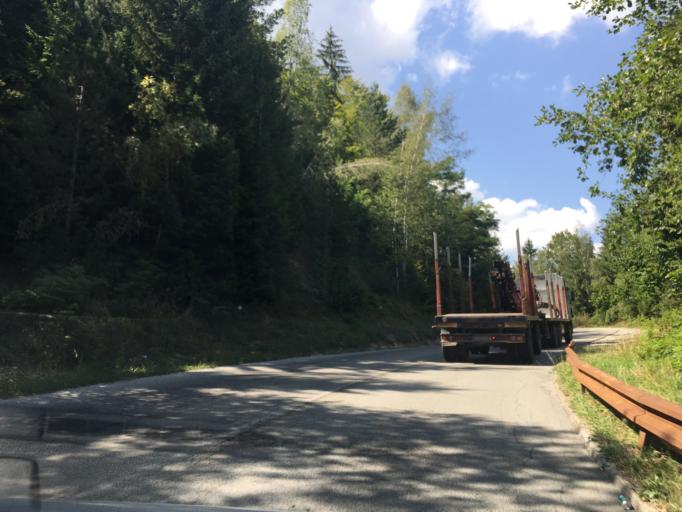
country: RS
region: Central Serbia
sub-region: Zlatiborski Okrug
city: Prijepolje
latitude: 43.3299
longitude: 19.5382
